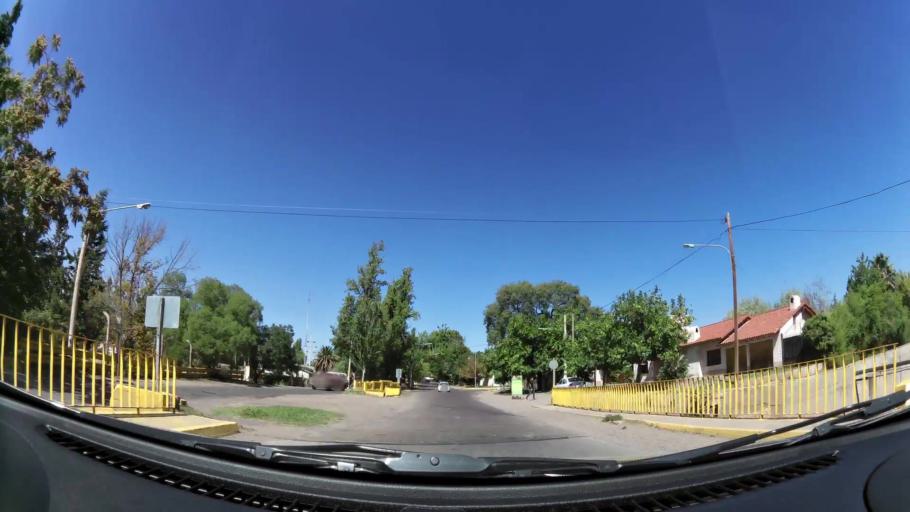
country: AR
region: Mendoza
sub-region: Departamento de Godoy Cruz
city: Godoy Cruz
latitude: -32.9579
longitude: -68.8535
